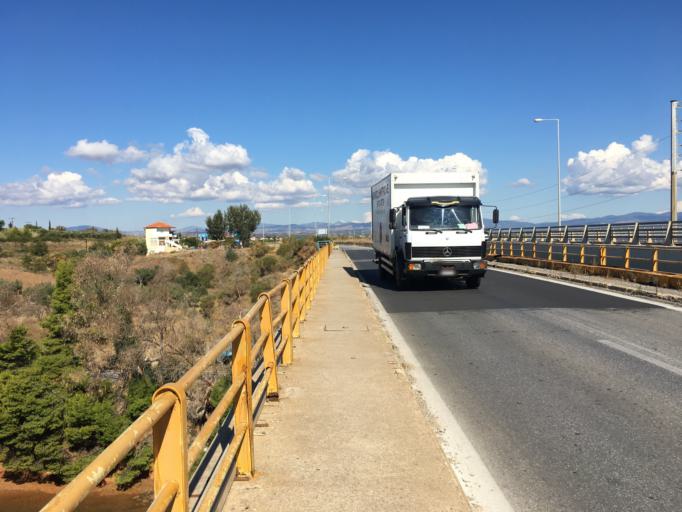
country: GR
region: Central Macedonia
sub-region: Nomos Chalkidikis
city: Nea Potidhaia
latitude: 40.1969
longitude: 23.3302
